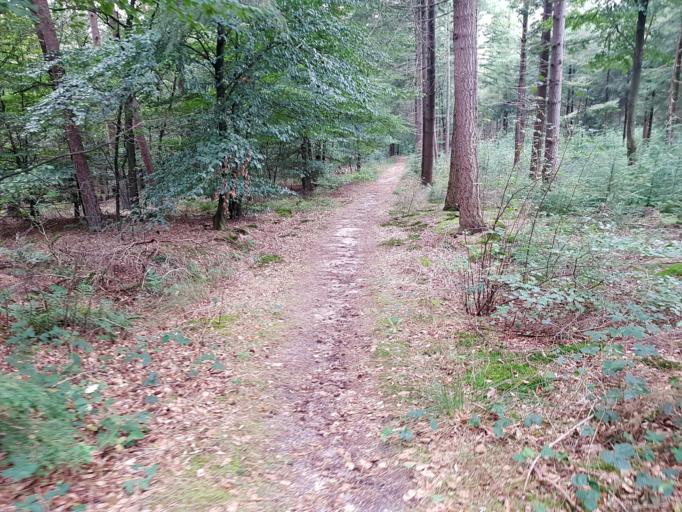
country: NL
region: Utrecht
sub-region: Gemeente Utrechtse Heuvelrug
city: Amerongen
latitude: 52.0210
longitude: 5.4708
